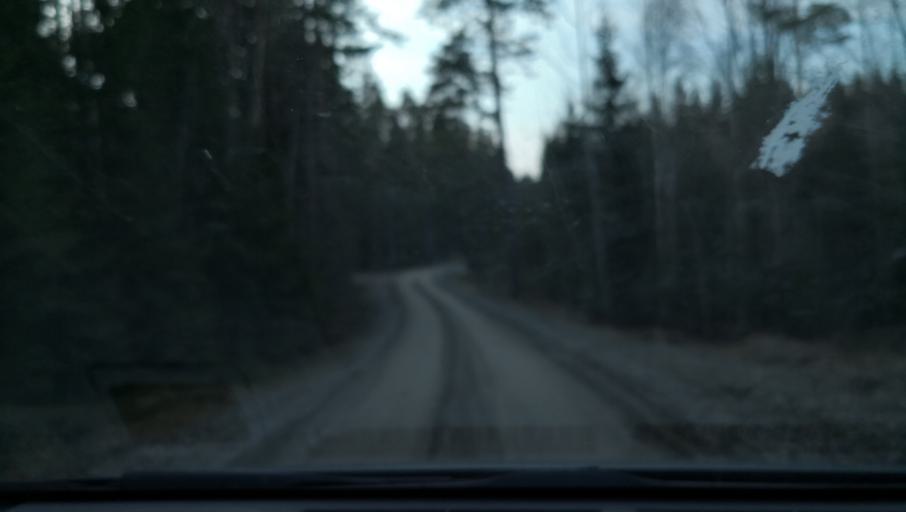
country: SE
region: OErebro
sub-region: Lindesbergs Kommun
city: Frovi
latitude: 59.3543
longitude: 15.3383
